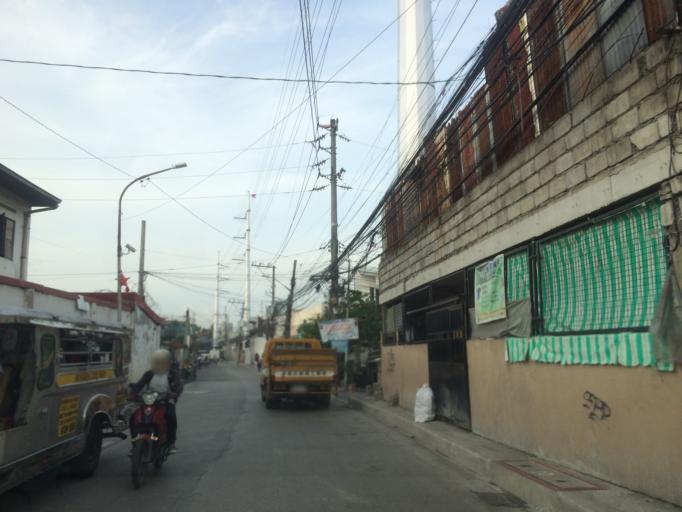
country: PH
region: Calabarzon
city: Del Monte
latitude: 14.6468
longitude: 121.0088
